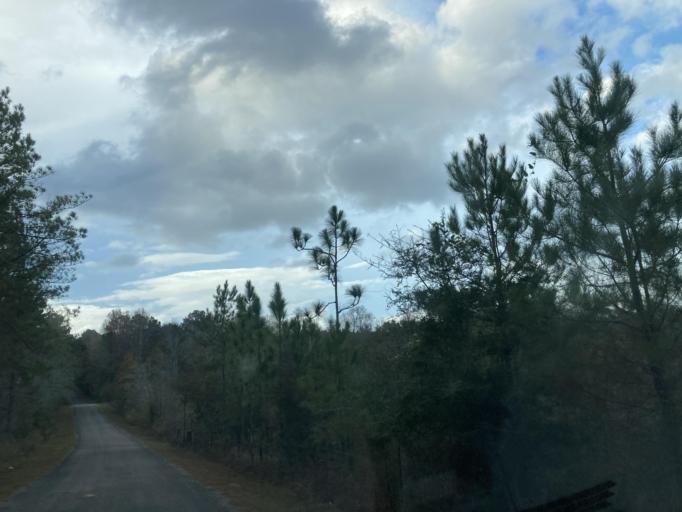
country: US
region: Mississippi
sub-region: Marion County
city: Columbia
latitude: 31.1859
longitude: -89.6463
